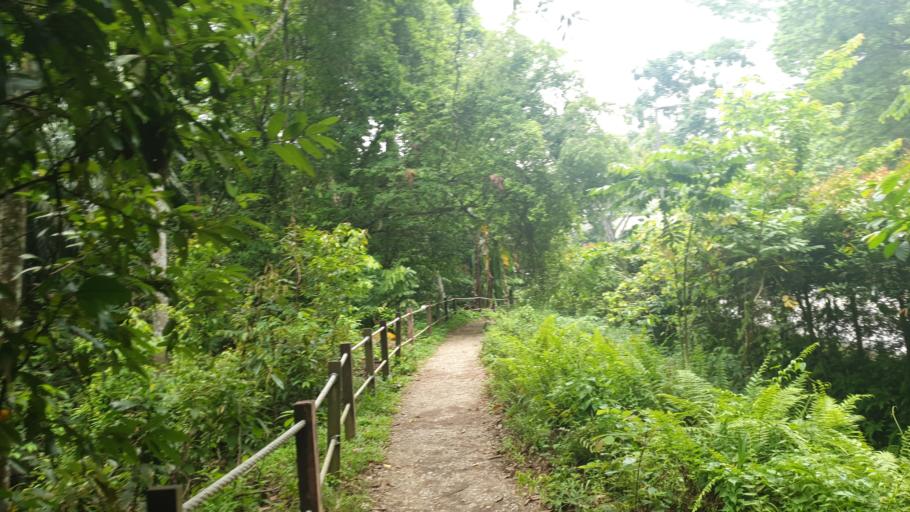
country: SG
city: Singapore
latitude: 1.3592
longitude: 103.8203
